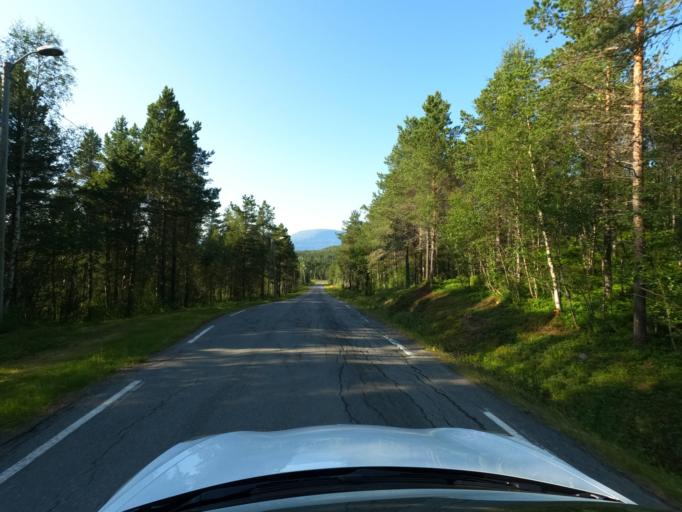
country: NO
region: Nordland
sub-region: Narvik
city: Bjerkvik
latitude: 68.4798
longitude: 17.5277
